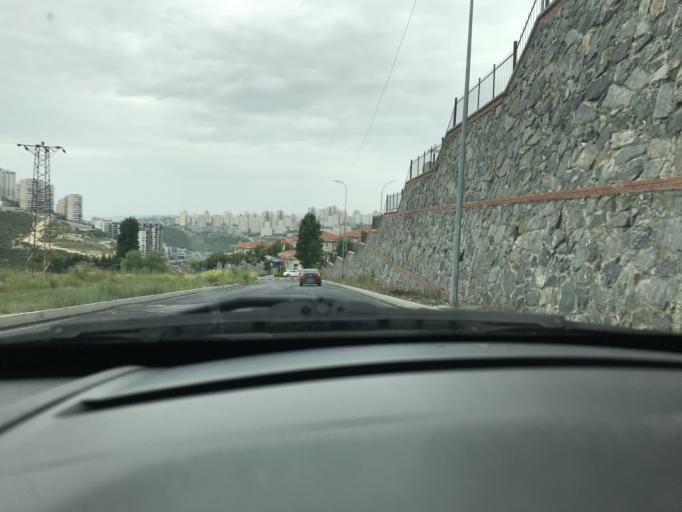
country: TR
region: Istanbul
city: Esenyurt
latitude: 41.0910
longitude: 28.6818
